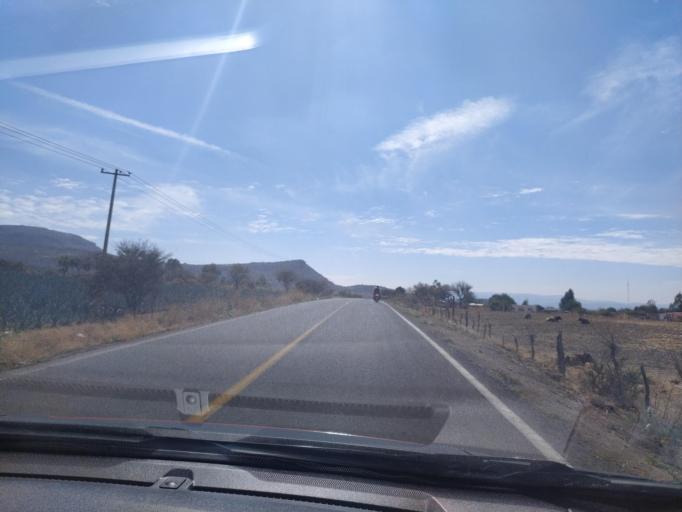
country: MX
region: Guanajuato
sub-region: San Francisco del Rincon
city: San Ignacio de Hidalgo
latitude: 20.8240
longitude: -101.8423
